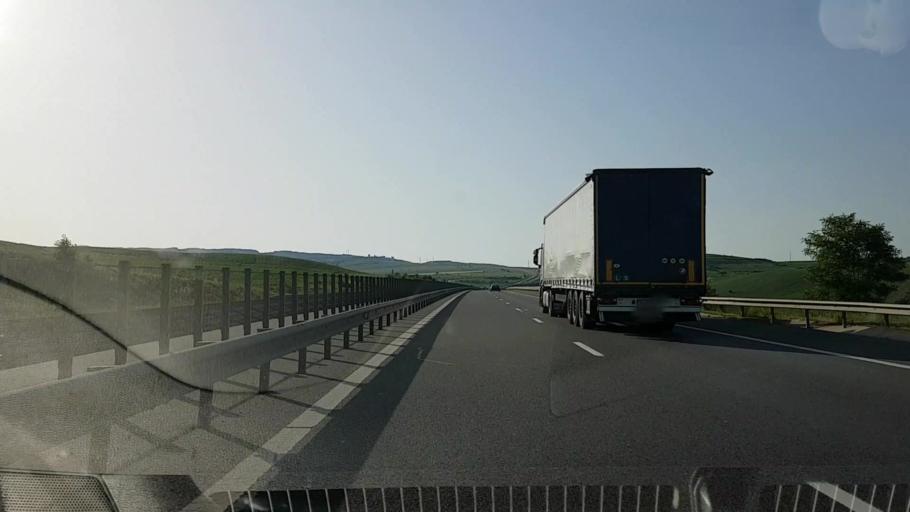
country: RO
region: Cluj
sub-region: Comuna Sandulesti
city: Copaceni
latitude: 46.5705
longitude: 23.7520
